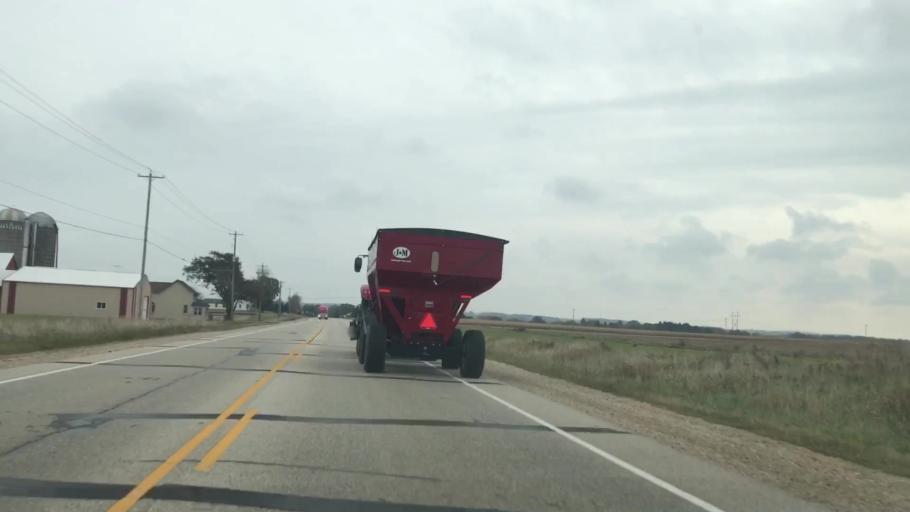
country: US
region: Wisconsin
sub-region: Washington County
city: Hartford
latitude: 43.4214
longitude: -88.3658
